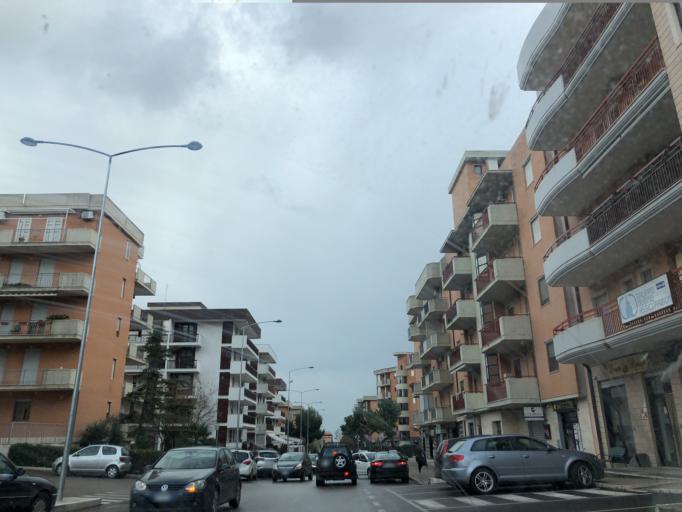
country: IT
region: Apulia
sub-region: Provincia di Foggia
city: Lucera
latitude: 41.5015
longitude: 15.3460
